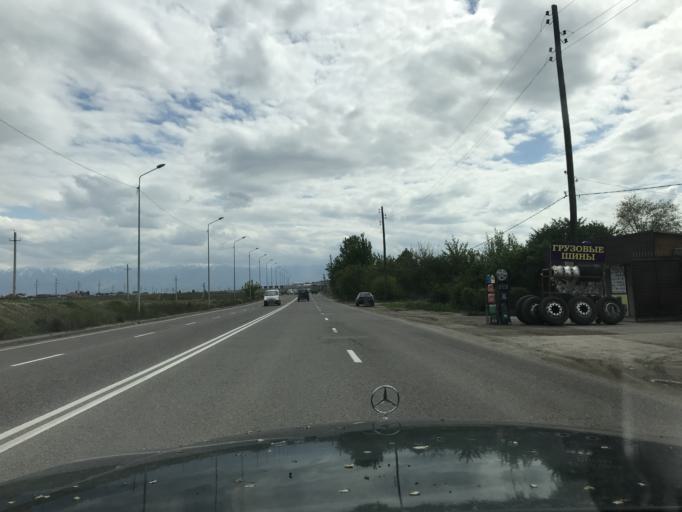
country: KZ
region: Almaty Oblysy
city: Burunday
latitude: 43.3526
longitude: 76.8347
